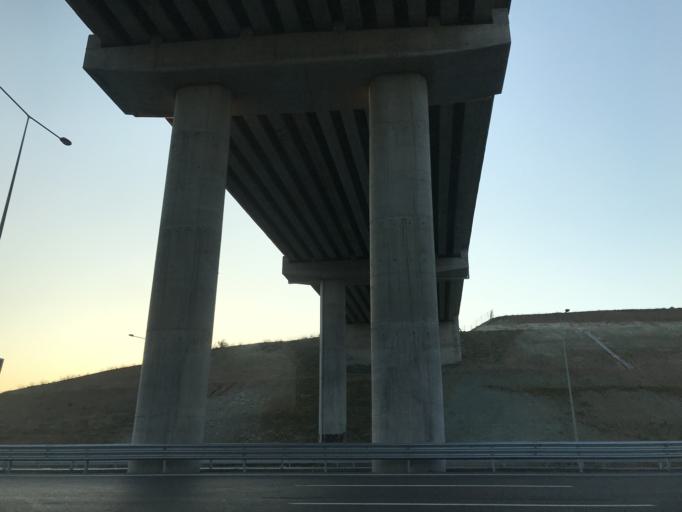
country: TR
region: Kocaeli
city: Tavsanli
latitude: 40.8060
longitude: 29.5199
